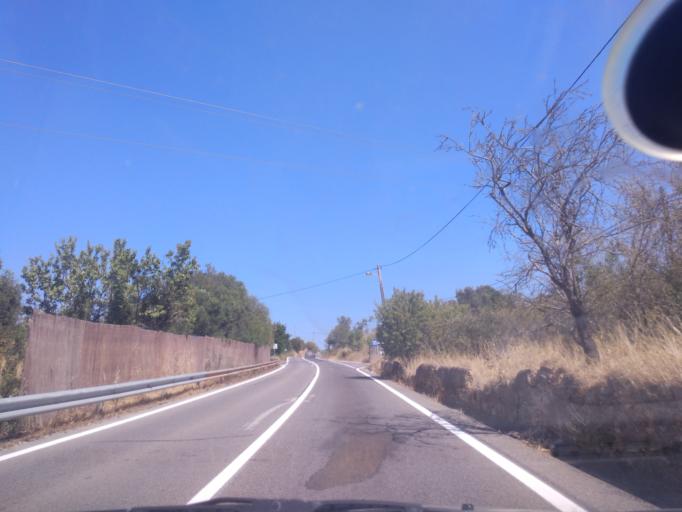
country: PT
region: Faro
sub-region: Lagos
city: Lagos
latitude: 37.1178
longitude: -8.6911
